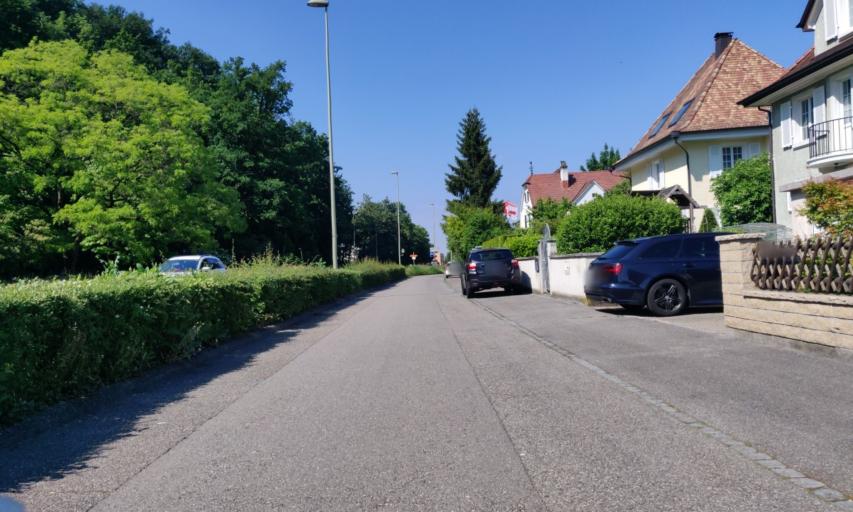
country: CH
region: Basel-Landschaft
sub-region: Bezirk Arlesheim
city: Munchenstein
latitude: 47.5202
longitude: 7.6029
